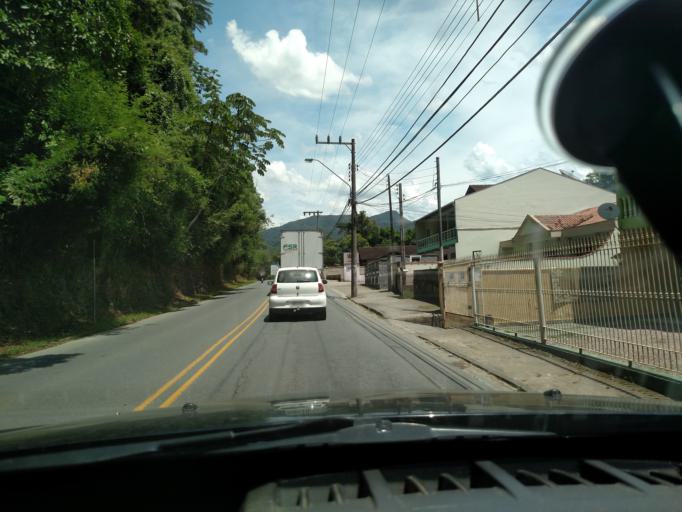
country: BR
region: Santa Catarina
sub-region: Blumenau
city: Blumenau
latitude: -26.9747
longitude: -49.0768
